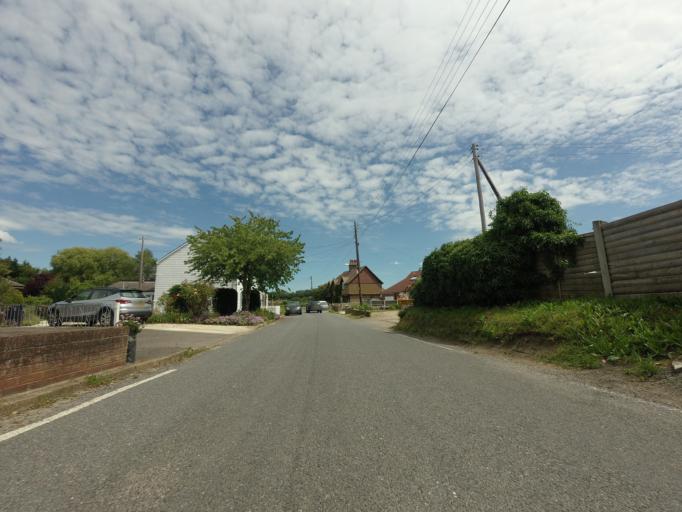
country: GB
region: England
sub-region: Kent
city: Strood
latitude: 51.4299
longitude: 0.4704
